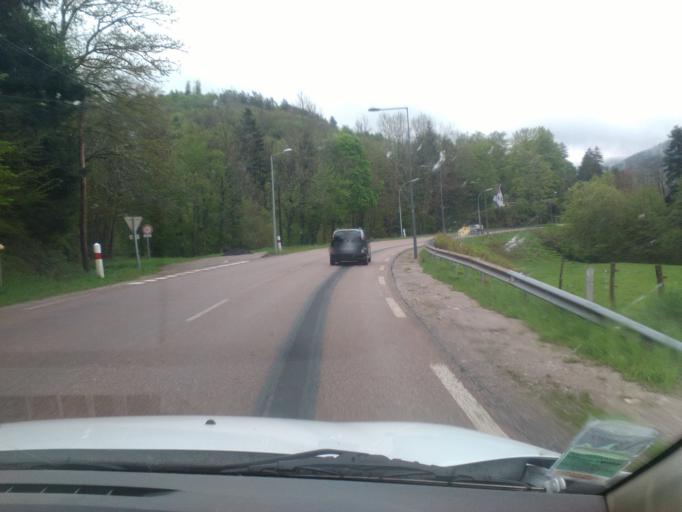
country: FR
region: Lorraine
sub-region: Departement des Vosges
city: Saulxures-sur-Moselotte
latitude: 47.9677
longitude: 6.7352
